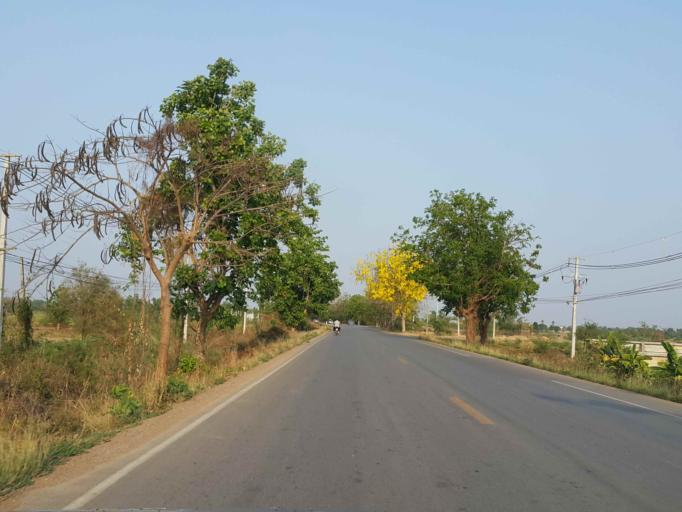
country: TH
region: Sukhothai
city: Sawankhalok
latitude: 17.3099
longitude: 99.8067
